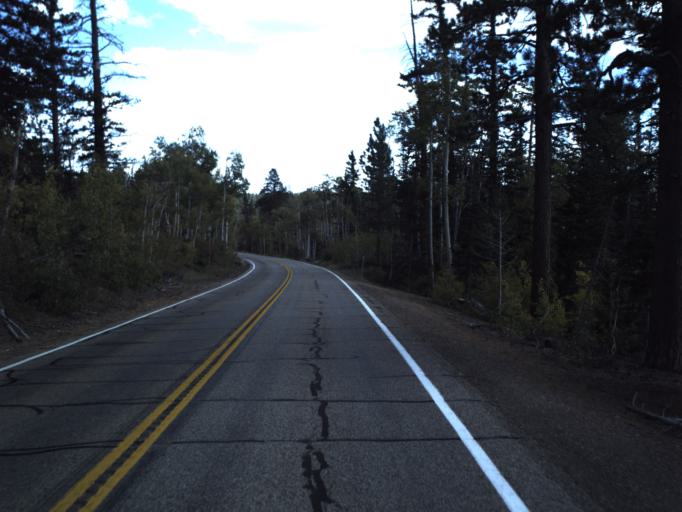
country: US
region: Utah
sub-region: Iron County
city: Parowan
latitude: 37.5194
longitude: -112.7255
